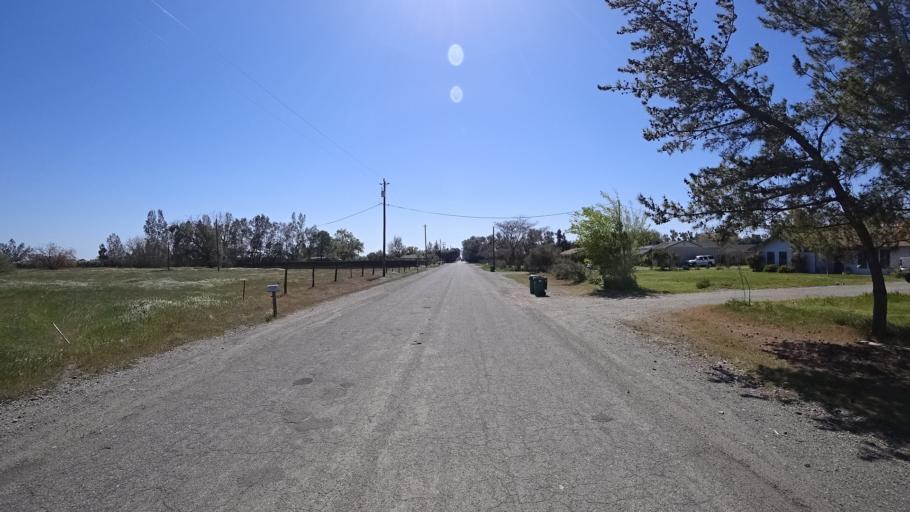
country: US
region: California
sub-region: Glenn County
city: Orland
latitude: 39.7746
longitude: -122.2386
